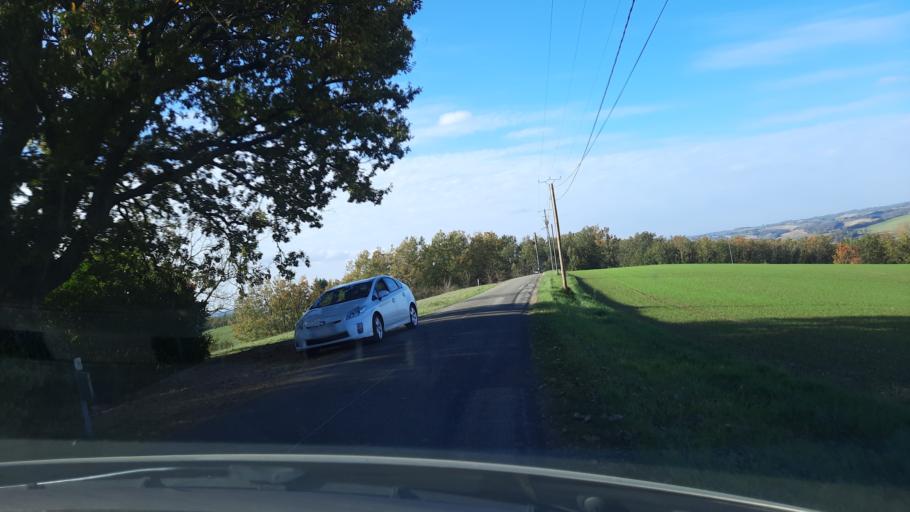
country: FR
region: Midi-Pyrenees
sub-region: Departement du Tarn-et-Garonne
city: Lafrancaise
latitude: 44.1473
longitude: 1.3003
